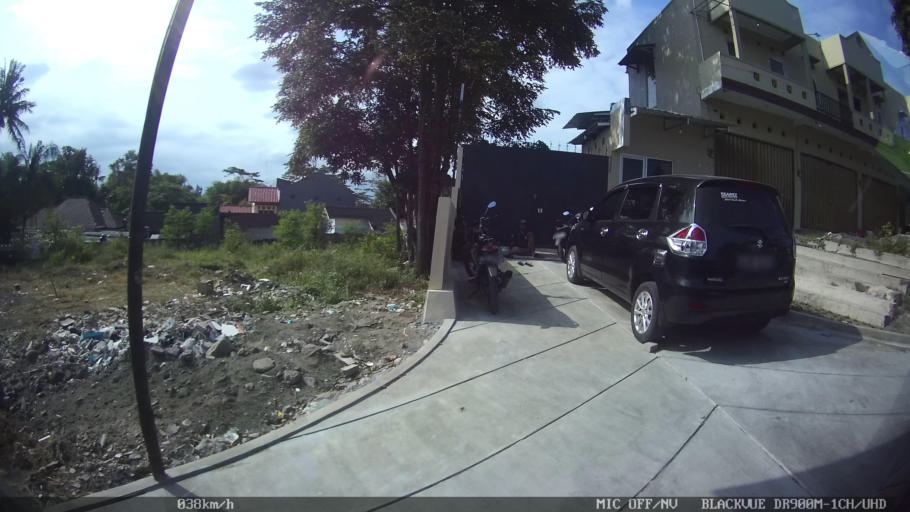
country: ID
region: Daerah Istimewa Yogyakarta
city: Depok
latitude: -7.7535
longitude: 110.4479
